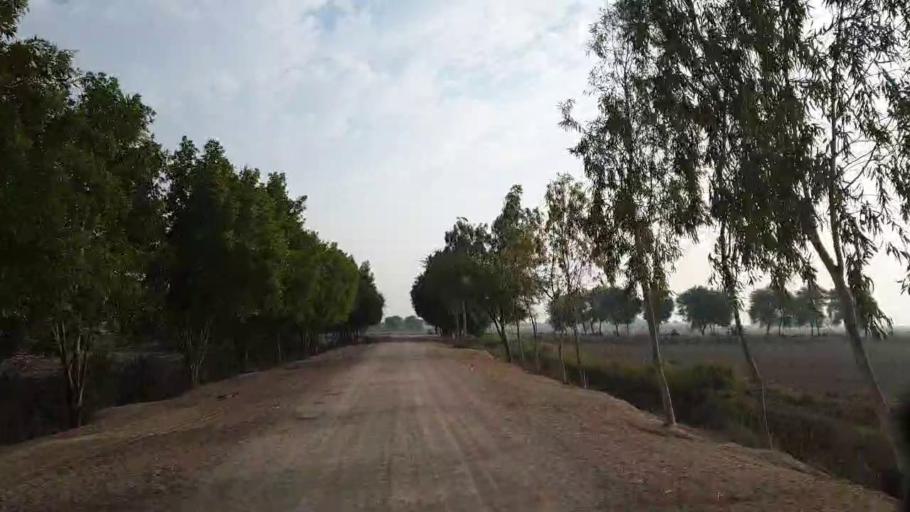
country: PK
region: Sindh
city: Tando Muhammad Khan
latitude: 25.1118
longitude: 68.4329
